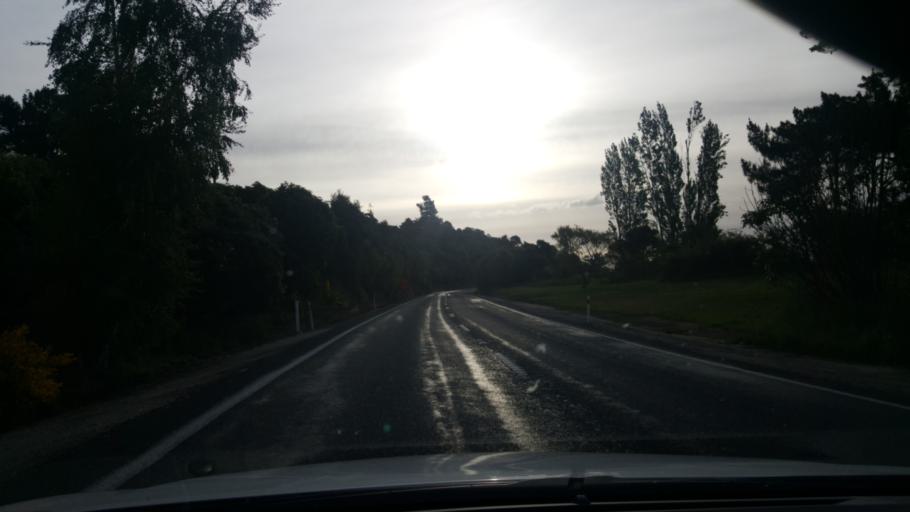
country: NZ
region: Waikato
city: Turangi
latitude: -38.9053
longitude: 175.9387
